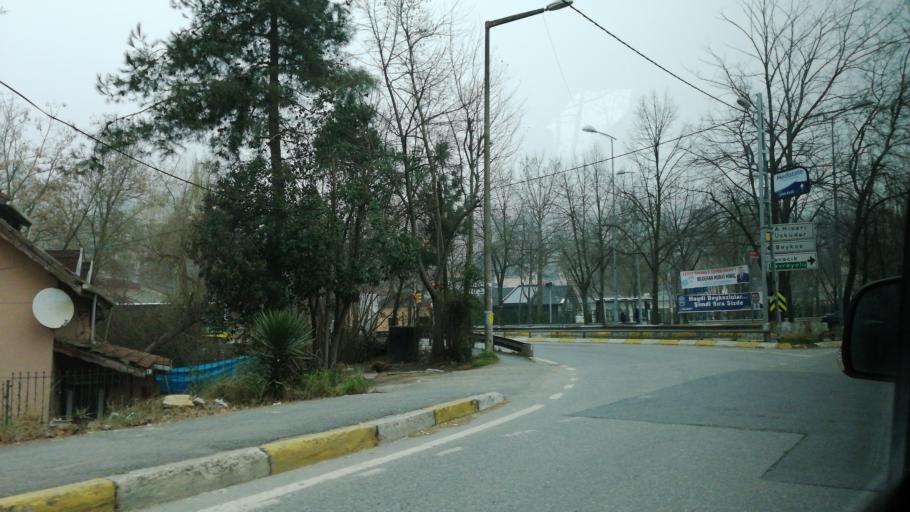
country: TR
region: Istanbul
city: UEskuedar
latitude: 41.0799
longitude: 29.0762
